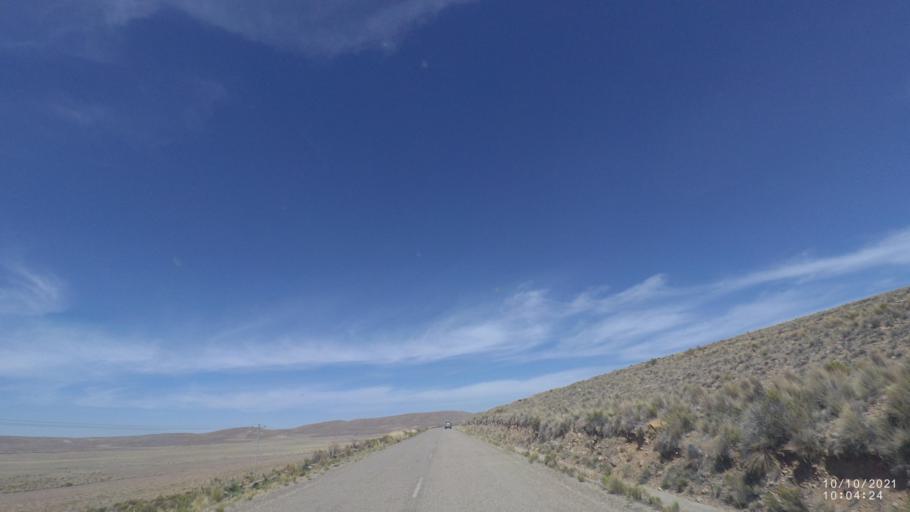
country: BO
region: La Paz
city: Eucaliptus
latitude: -17.3819
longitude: -67.4456
